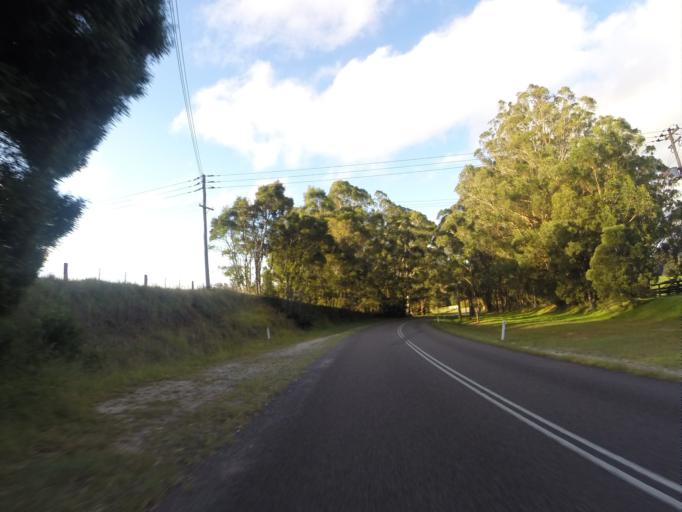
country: AU
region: New South Wales
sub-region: Shoalhaven Shire
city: Kangaroo Valley
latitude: -34.6187
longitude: 150.5297
